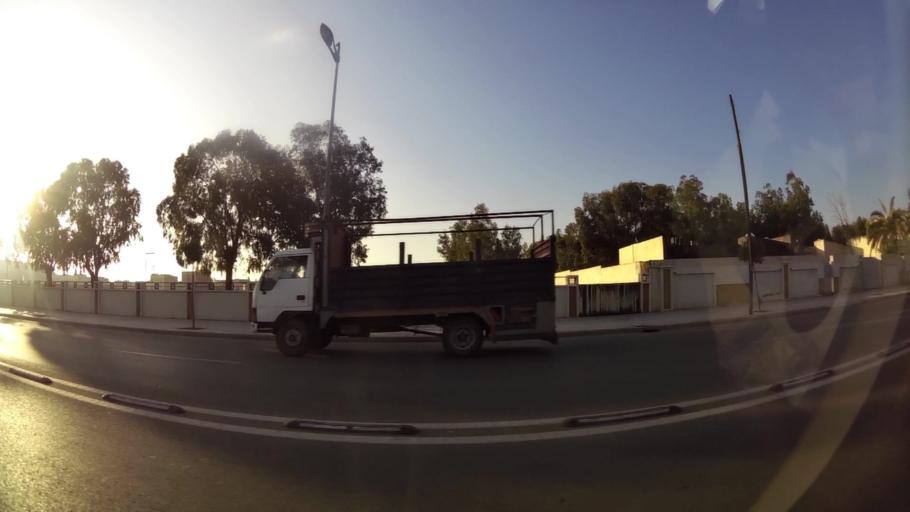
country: MA
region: Oriental
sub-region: Oujda-Angad
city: Oujda
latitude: 34.6728
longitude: -1.9336
